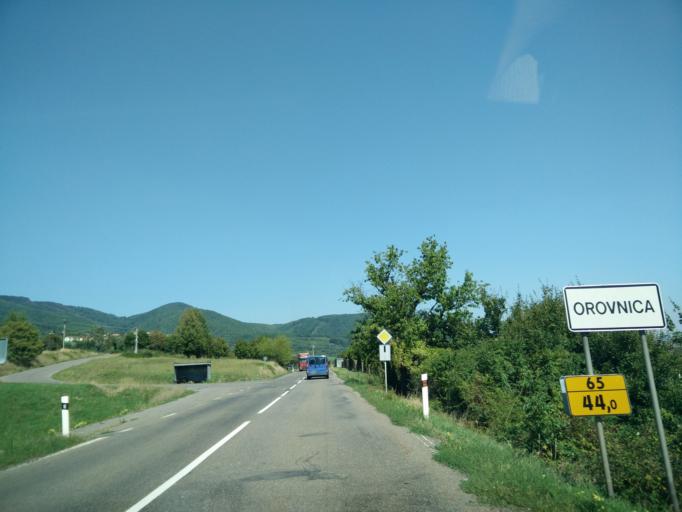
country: SK
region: Banskobystricky
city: Nova Bana
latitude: 48.3765
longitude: 18.5984
